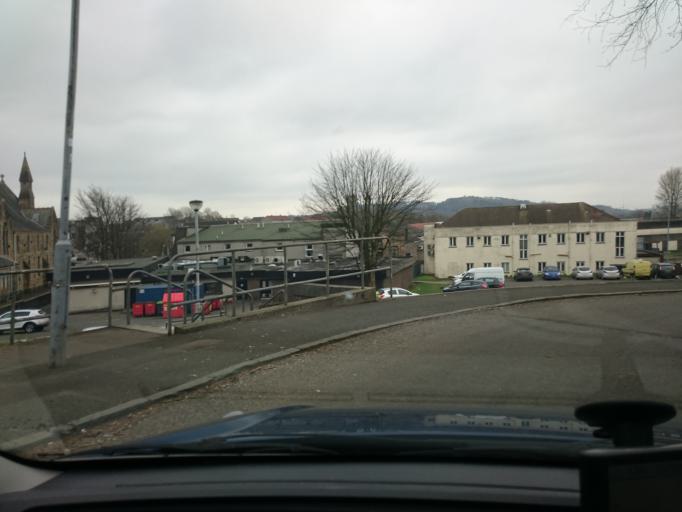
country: GB
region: Scotland
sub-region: North Lanarkshire
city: Kilsyth
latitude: 55.9793
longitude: -4.0585
